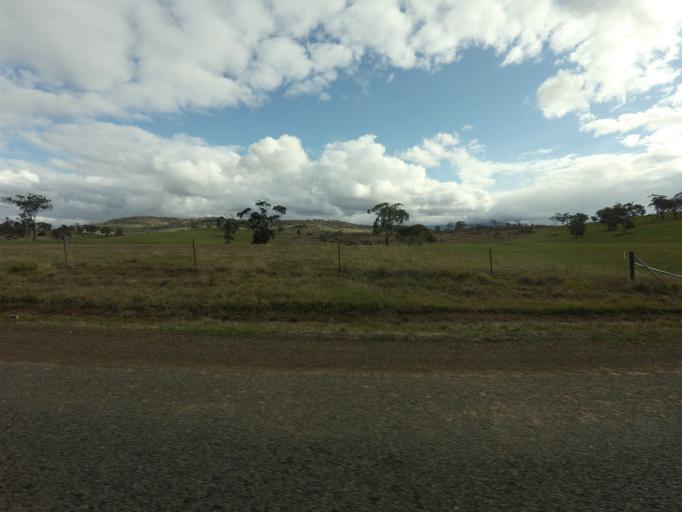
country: AU
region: Tasmania
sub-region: Northern Midlands
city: Evandale
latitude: -41.8824
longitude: 147.3091
